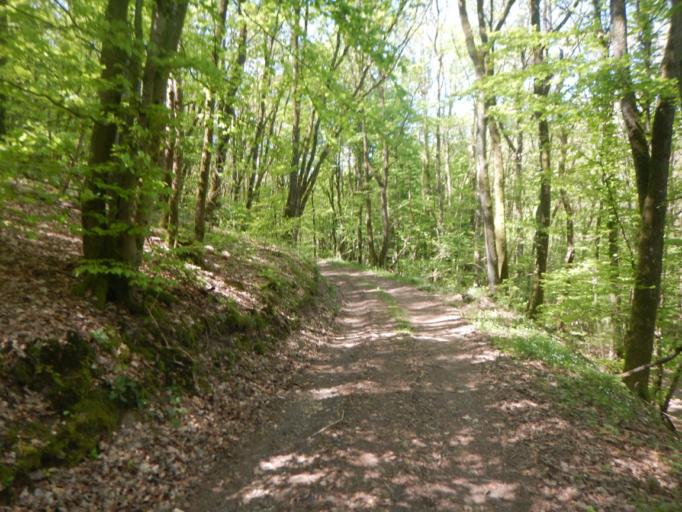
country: LU
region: Diekirch
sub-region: Canton de Diekirch
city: Bourscheid
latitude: 49.8910
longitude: 6.0920
